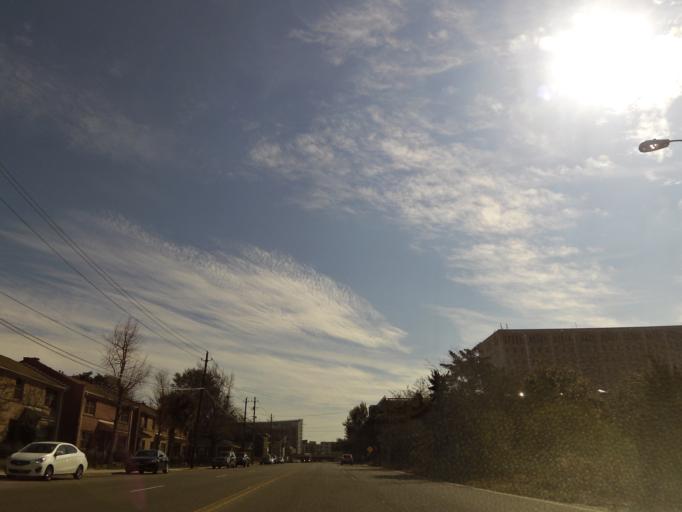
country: US
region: South Carolina
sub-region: Charleston County
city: Charleston
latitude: 32.7895
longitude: -79.9554
